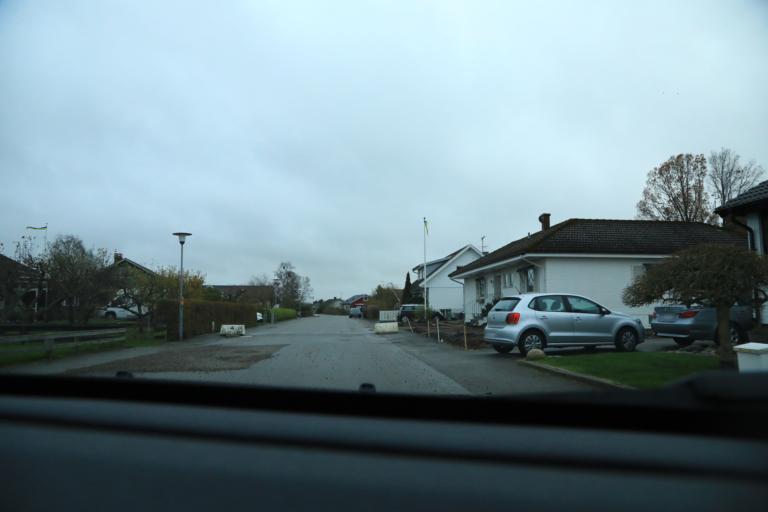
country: SE
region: Halland
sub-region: Varbergs Kommun
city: Varberg
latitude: 57.1740
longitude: 12.2225
